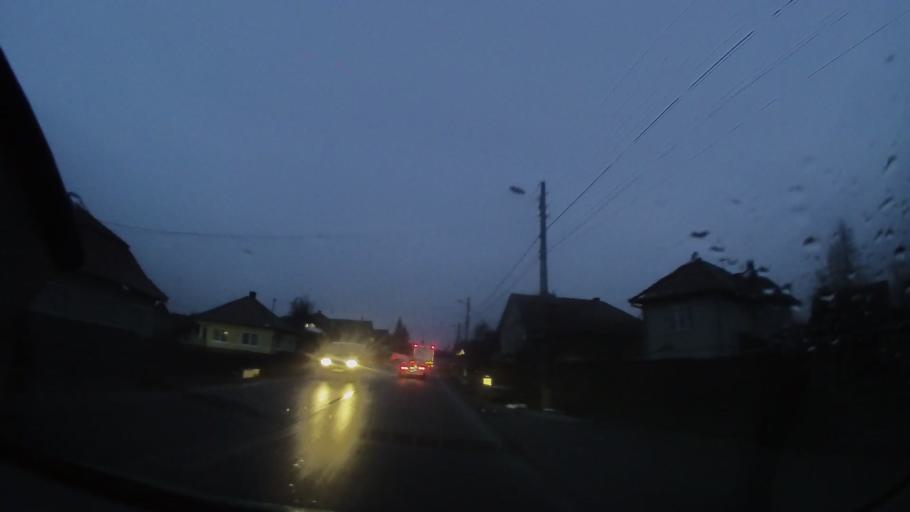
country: RO
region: Harghita
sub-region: Comuna Ditrau
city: Ditrau
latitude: 46.8108
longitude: 25.4940
